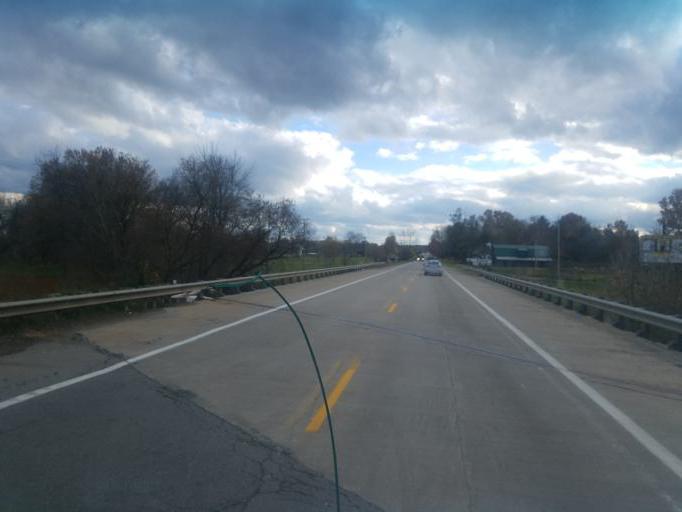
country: US
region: Ohio
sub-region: Wayne County
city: Orrville
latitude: 40.8125
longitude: -81.7654
